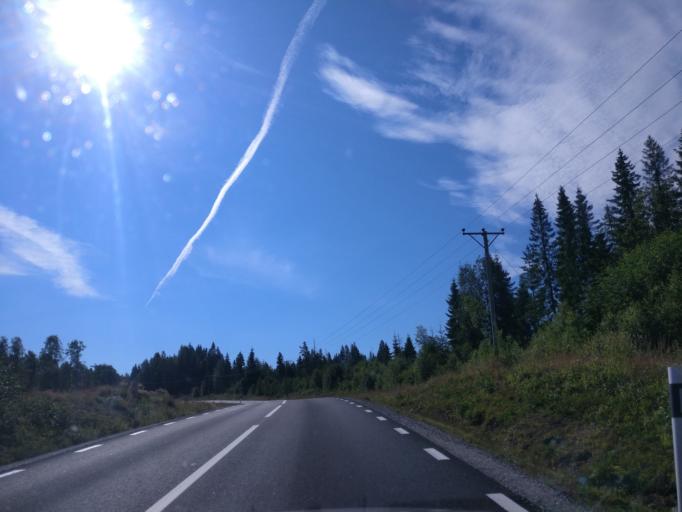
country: SE
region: Vaermland
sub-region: Hagfors Kommun
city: Hagfors
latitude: 60.0506
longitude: 13.7872
